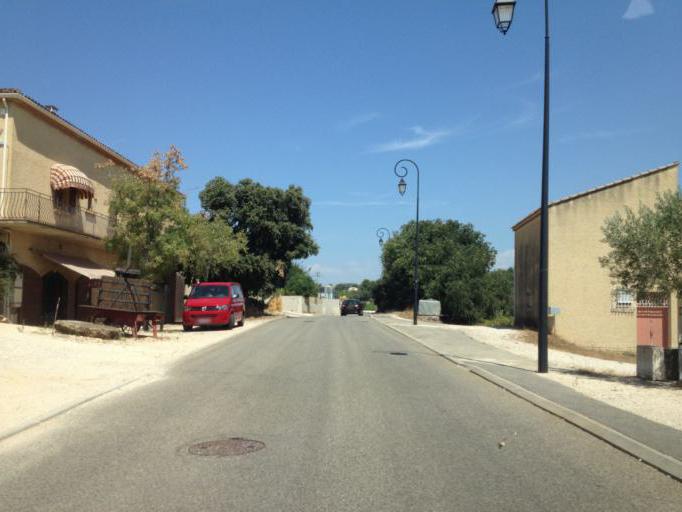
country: FR
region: Provence-Alpes-Cote d'Azur
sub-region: Departement du Vaucluse
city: Chateauneuf-du-Pape
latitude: 44.0609
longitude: 4.8390
